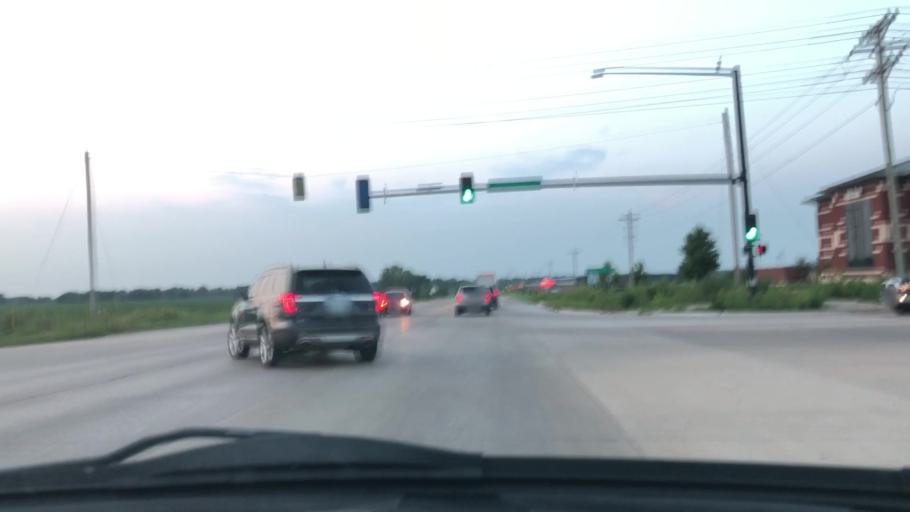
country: US
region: Iowa
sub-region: Johnson County
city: North Liberty
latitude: 41.7229
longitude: -91.6077
